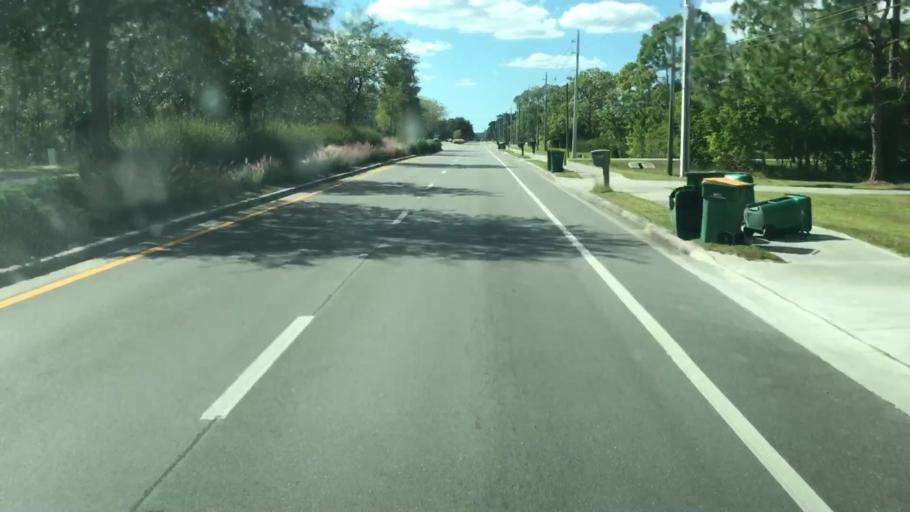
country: US
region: Florida
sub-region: Collier County
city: Vineyards
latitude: 26.2293
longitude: -81.6588
